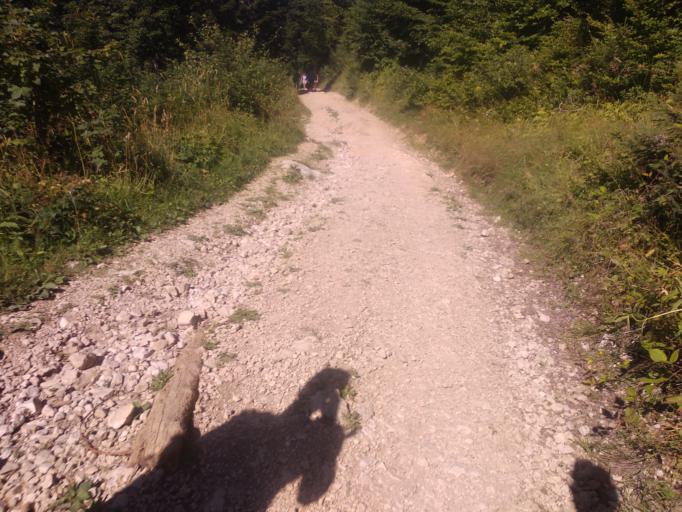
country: FR
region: Rhone-Alpes
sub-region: Departement de l'Isere
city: Le Sappey-en-Chartreuse
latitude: 45.2903
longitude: 5.7767
